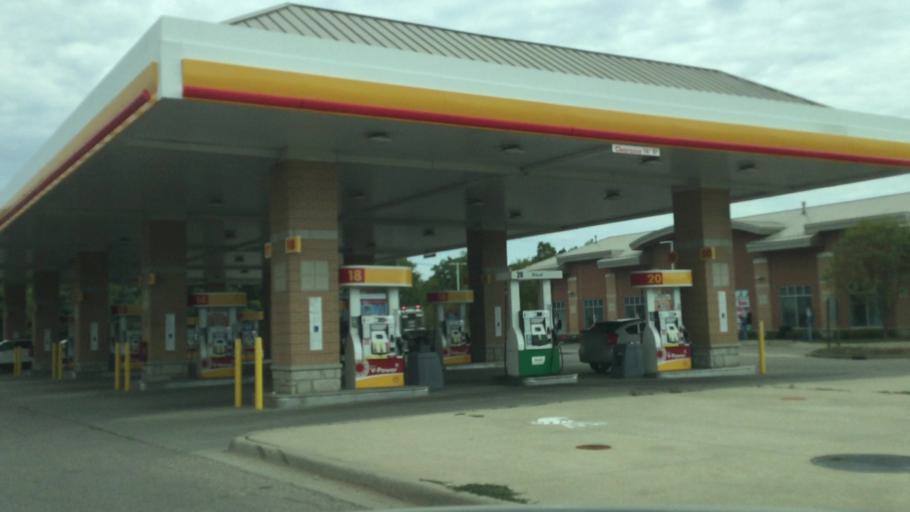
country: US
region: Michigan
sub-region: Livingston County
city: Howell
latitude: 42.6282
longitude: -83.8745
